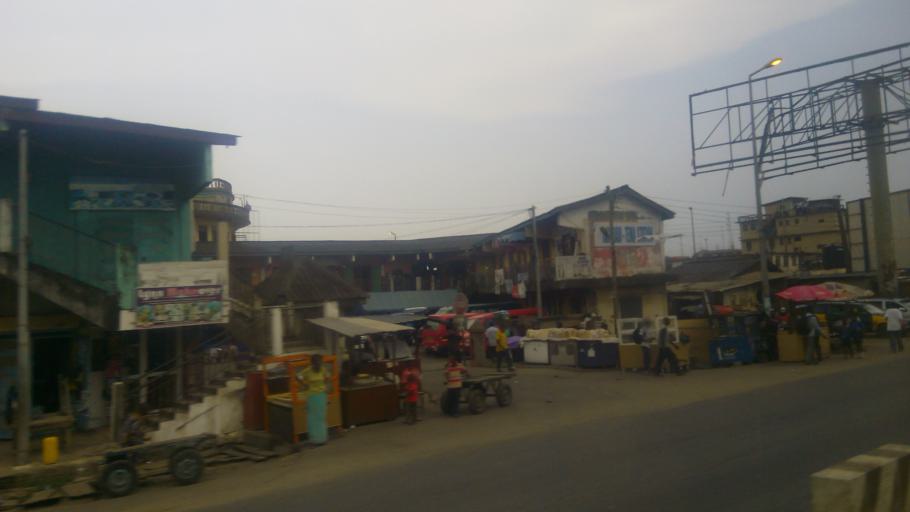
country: GH
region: Western
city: Takoradi
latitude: 4.8982
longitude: -1.7659
